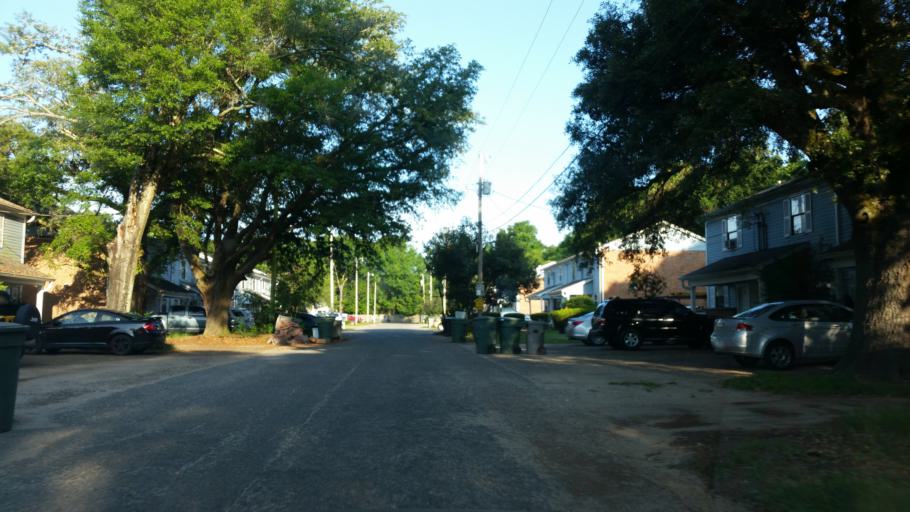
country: US
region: Florida
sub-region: Escambia County
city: Ferry Pass
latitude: 30.5054
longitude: -87.2072
